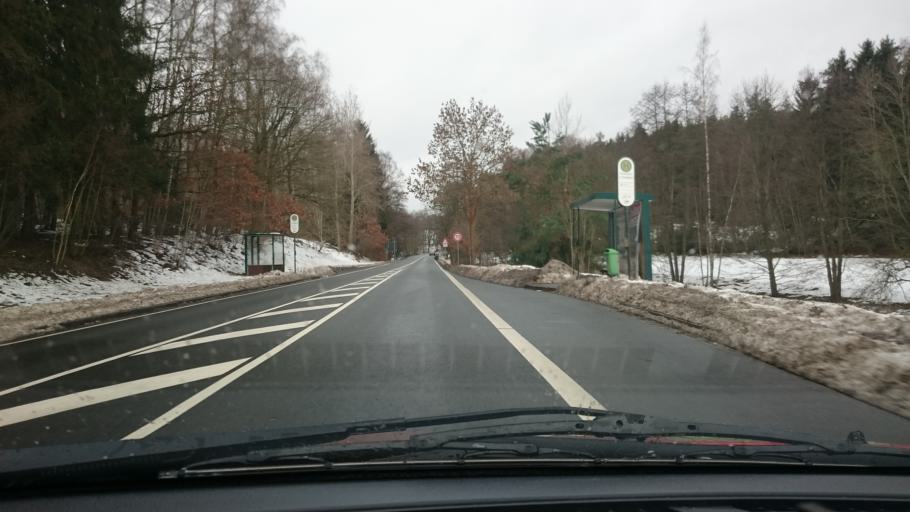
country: DE
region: Saxony
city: Waldkirchen
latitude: 50.5931
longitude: 12.4001
